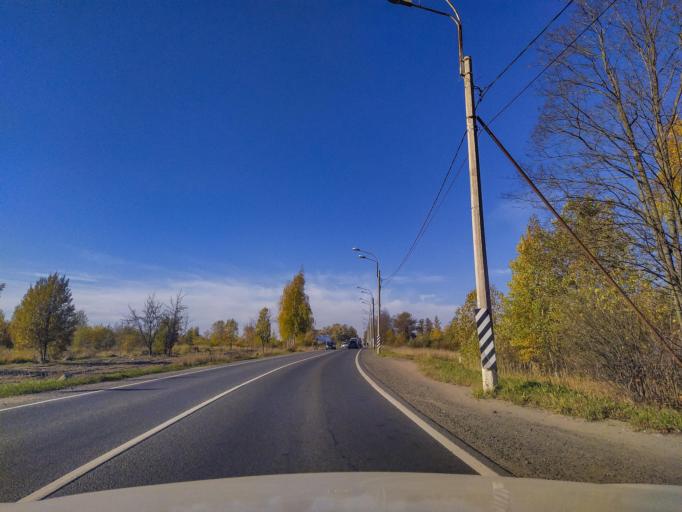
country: RU
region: St.-Petersburg
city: Aleksandrovskaya
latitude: 59.7036
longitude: 30.3496
